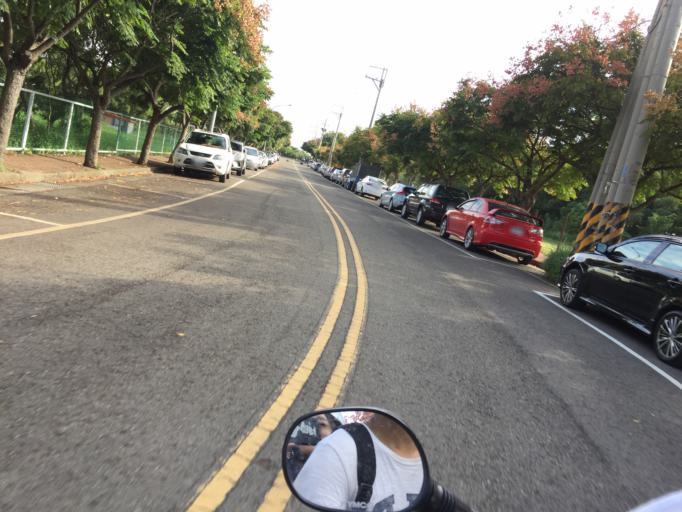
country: TW
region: Taiwan
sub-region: Hsinchu
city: Hsinchu
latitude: 24.7743
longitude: 120.9249
